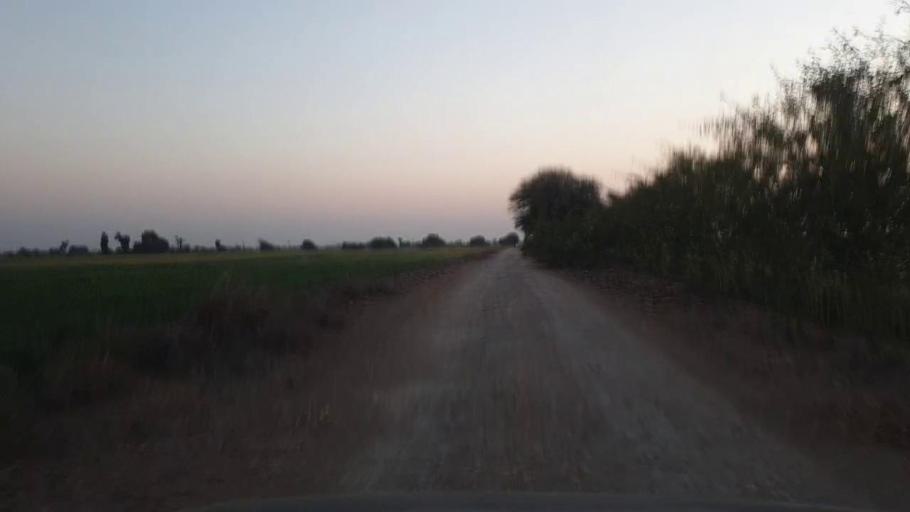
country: PK
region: Sindh
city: Digri
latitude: 25.1896
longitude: 69.1886
